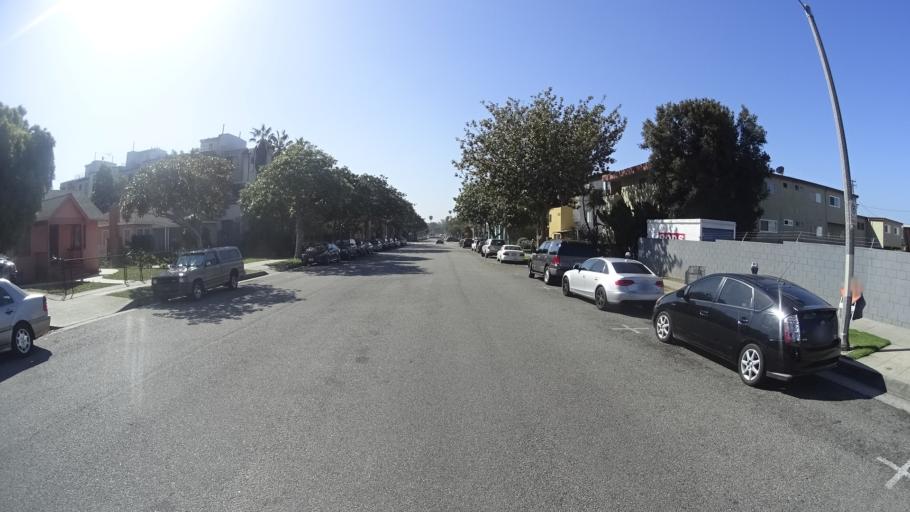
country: US
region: California
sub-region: Los Angeles County
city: Santa Monica
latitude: 34.0252
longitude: -118.4833
